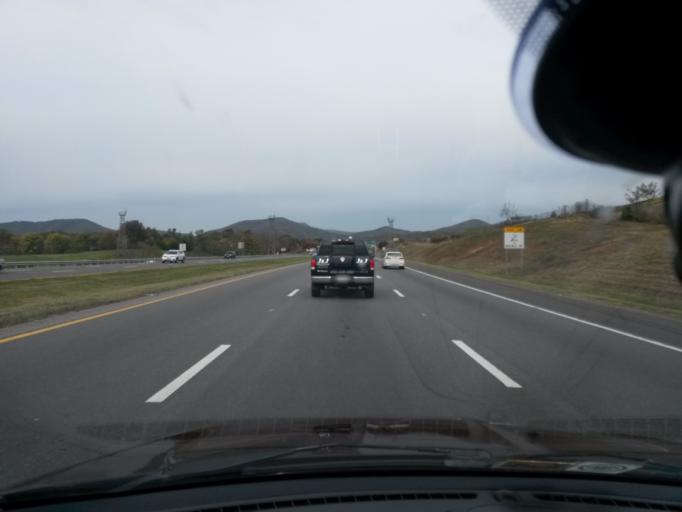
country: US
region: Virginia
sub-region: Roanoke County
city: Hollins
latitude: 37.3195
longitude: -79.9839
